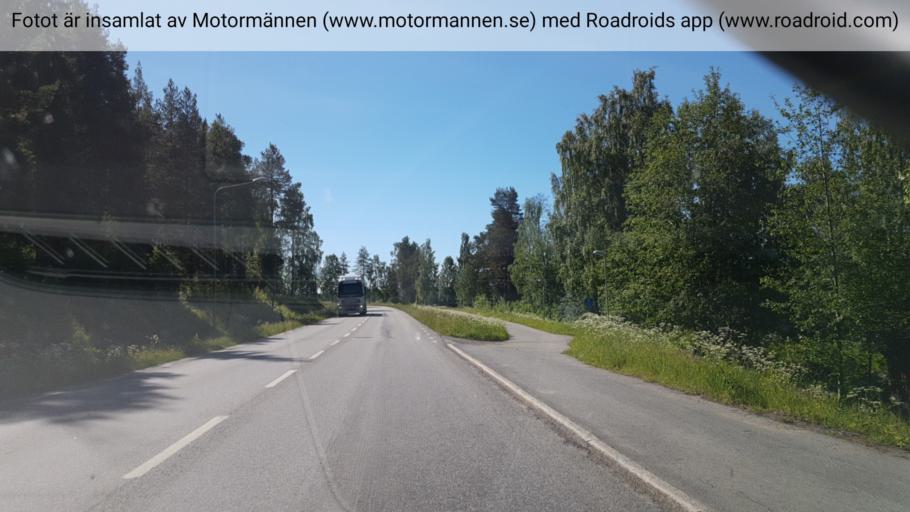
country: SE
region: Norrbotten
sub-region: Bodens Kommun
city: Boden
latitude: 65.8342
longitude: 21.6154
